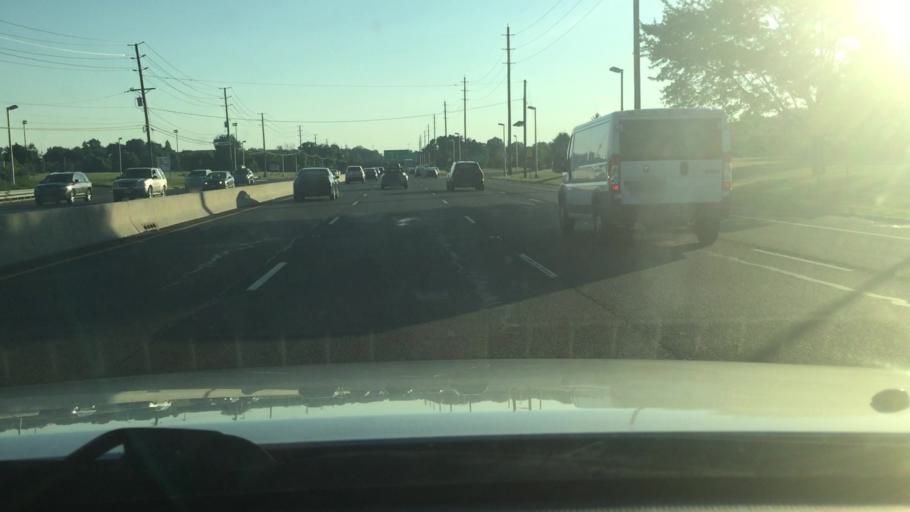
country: US
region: New Jersey
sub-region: Middlesex County
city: Milltown
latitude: 40.4667
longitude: -74.4410
